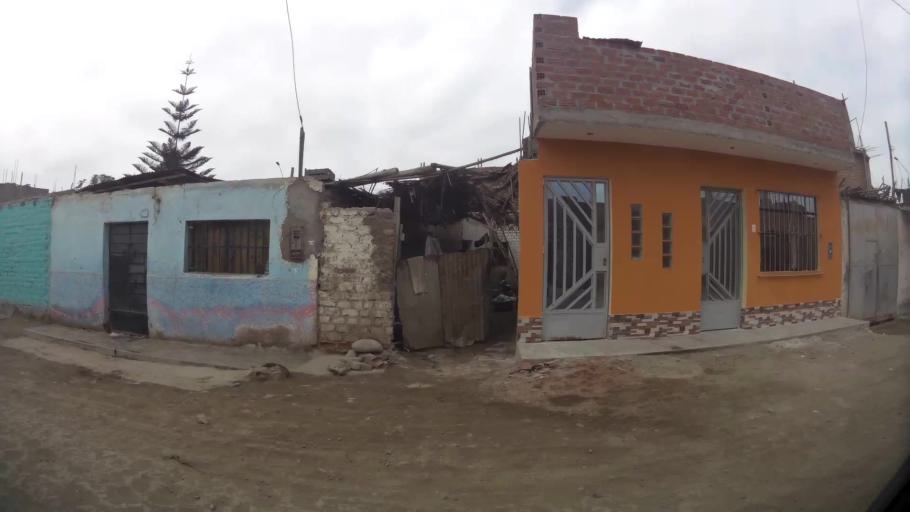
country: PE
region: Lima
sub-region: Provincia de Huaral
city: Huaral
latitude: -11.4898
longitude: -77.2103
